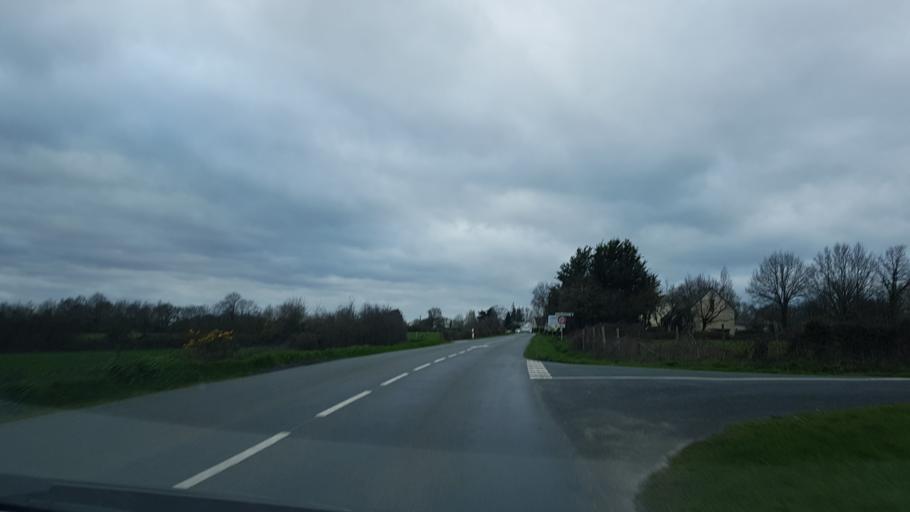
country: FR
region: Pays de la Loire
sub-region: Departement de la Loire-Atlantique
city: La Grigonnais
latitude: 47.5179
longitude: -1.6632
